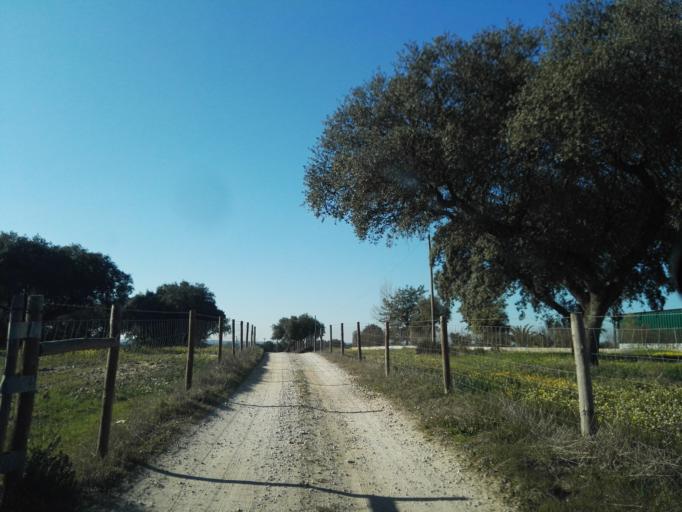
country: PT
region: Evora
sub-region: Evora
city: Evora
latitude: 38.5442
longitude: -7.9483
